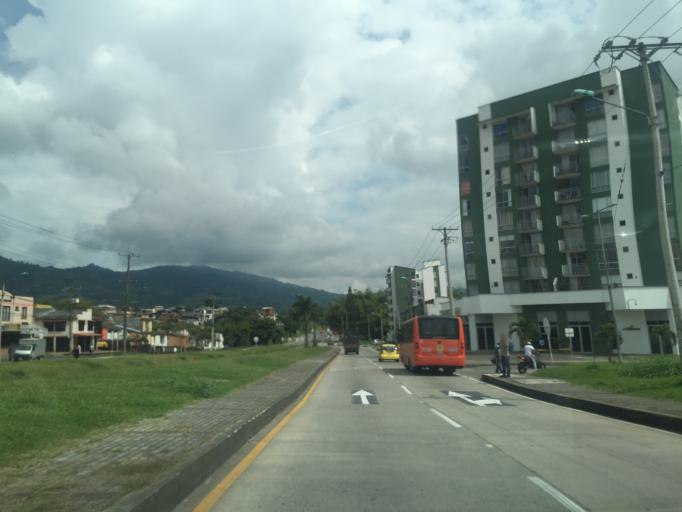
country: CO
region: Risaralda
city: Pereira
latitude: 4.8262
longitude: -75.6844
